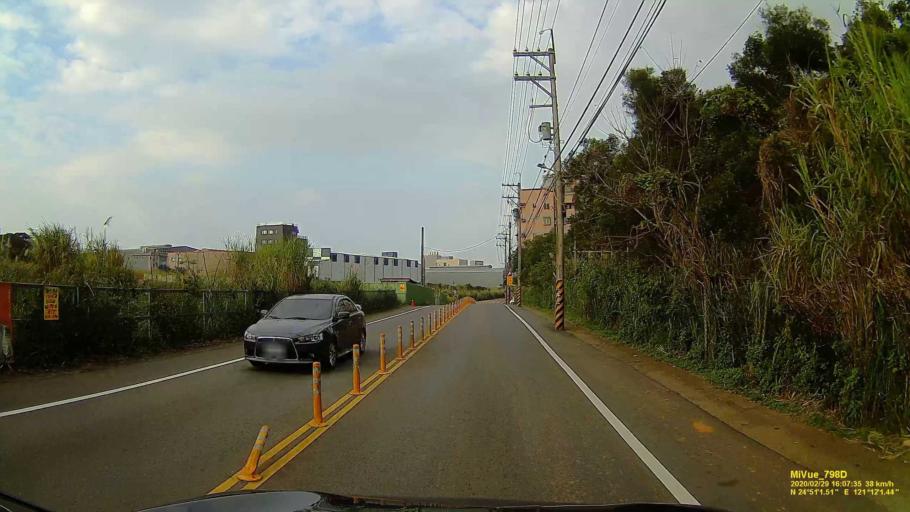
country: TW
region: Taiwan
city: Daxi
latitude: 24.8504
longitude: 121.2005
